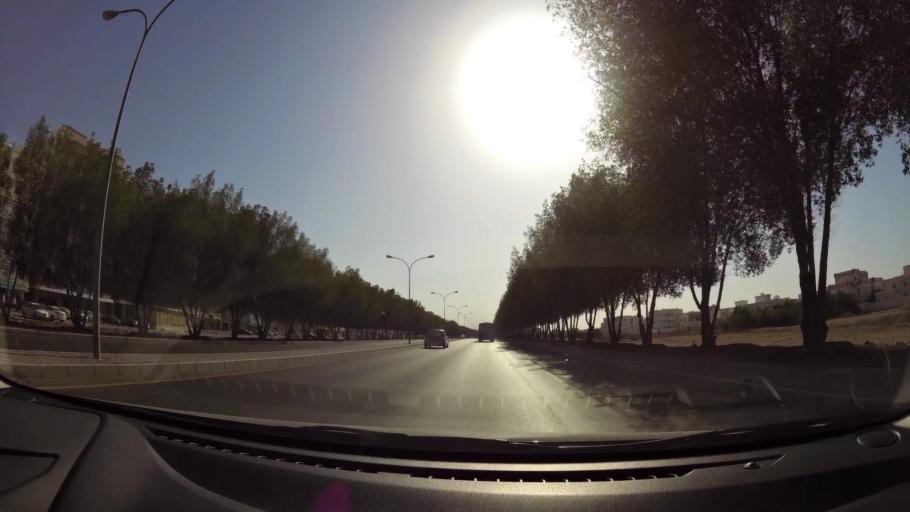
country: OM
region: Muhafazat Masqat
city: As Sib al Jadidah
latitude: 23.6157
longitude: 58.2047
